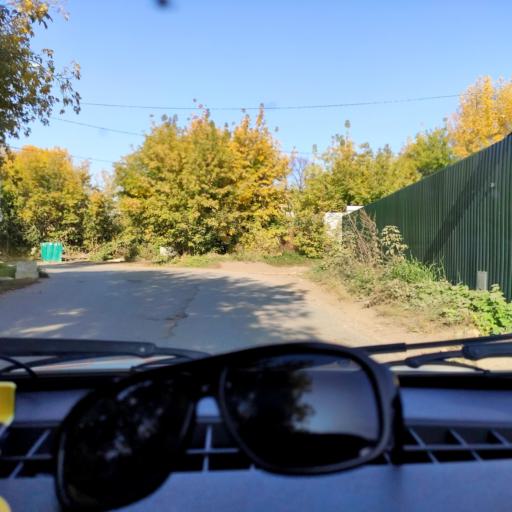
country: RU
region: Bashkortostan
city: Ufa
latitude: 54.7100
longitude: 55.9801
